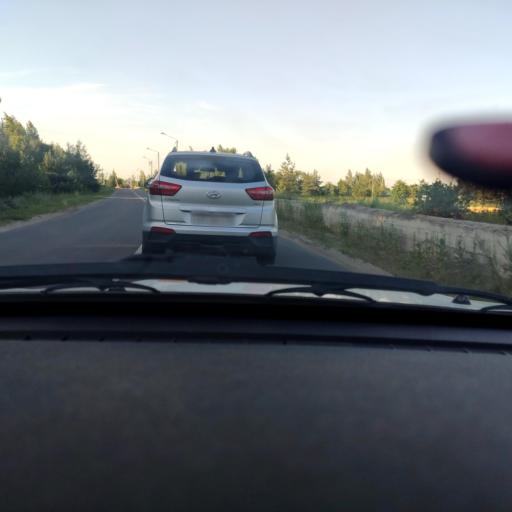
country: RU
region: Voronezj
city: Ramon'
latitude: 51.8886
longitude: 39.2513
